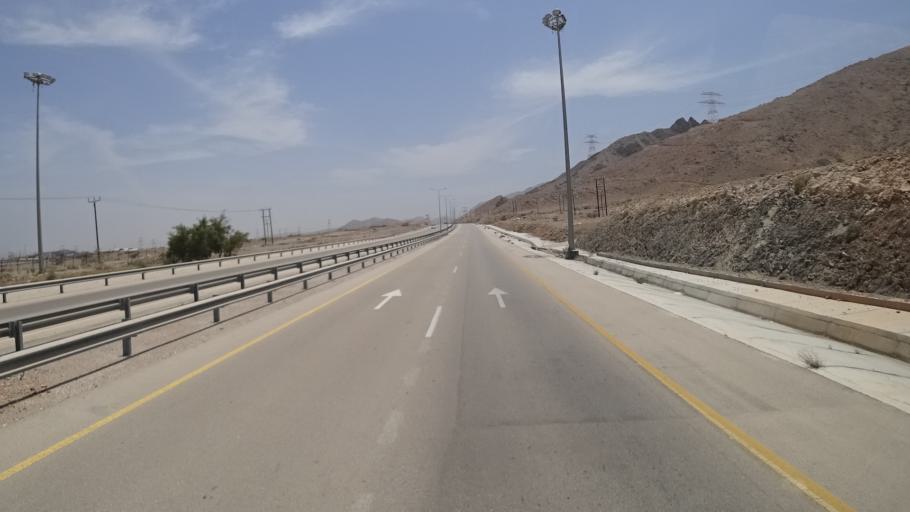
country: OM
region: Ash Sharqiyah
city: Sur
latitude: 22.6660
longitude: 59.3897
